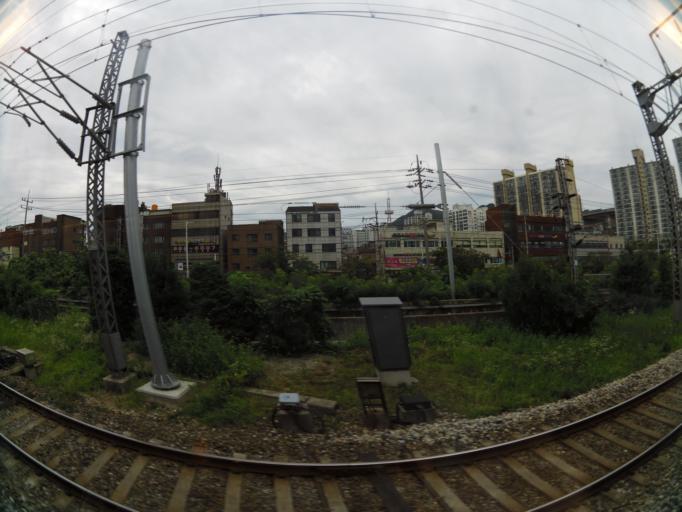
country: KR
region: Gyeonggi-do
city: Anyang-si
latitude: 37.3750
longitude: 126.9418
